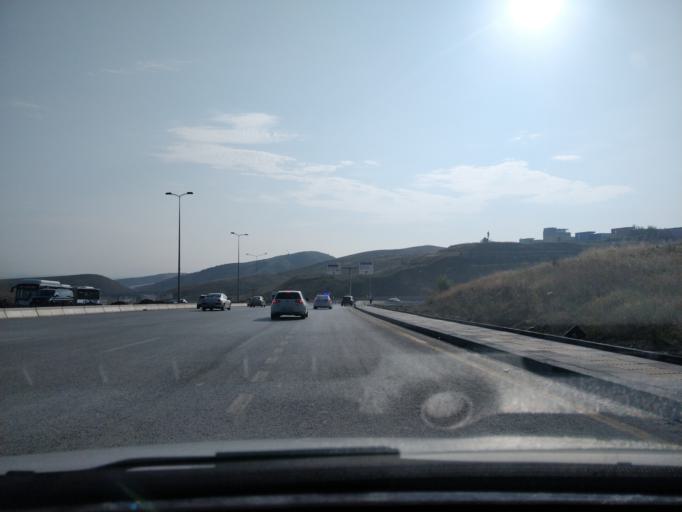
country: TR
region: Ankara
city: Etimesgut
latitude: 39.8979
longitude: 32.6736
